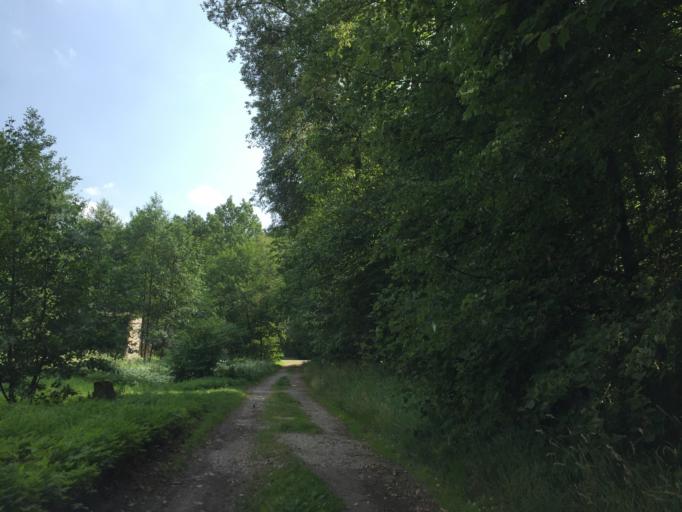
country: LV
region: Jelgava
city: Jelgava
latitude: 56.6849
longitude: 23.7212
